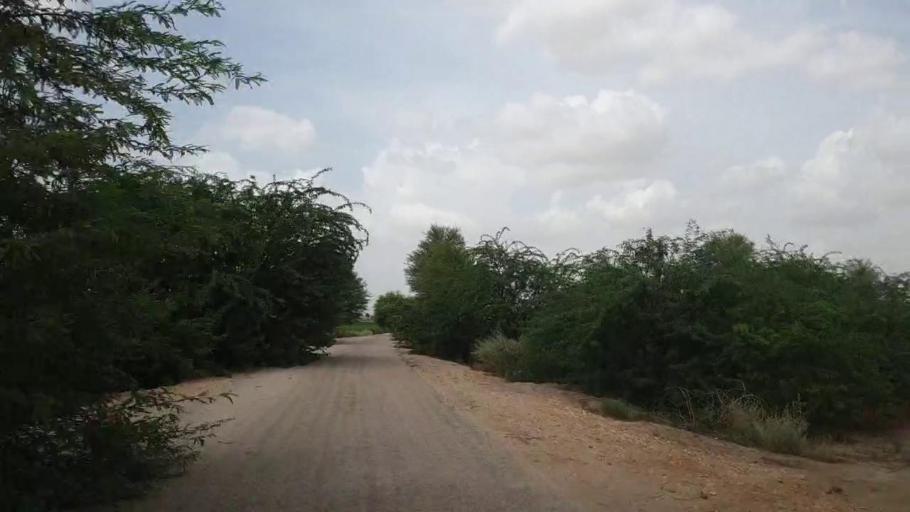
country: PK
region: Sindh
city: Kot Diji
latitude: 27.2210
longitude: 69.0842
